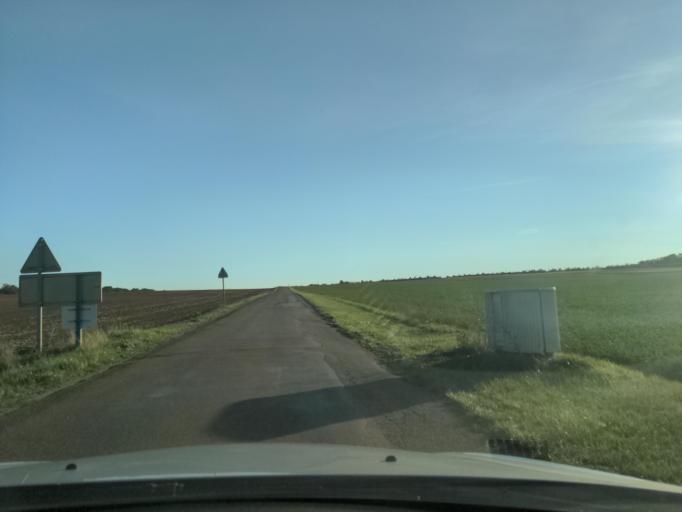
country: FR
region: Bourgogne
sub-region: Departement de la Cote-d'Or
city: Ruffey-les-Echirey
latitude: 47.3958
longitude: 5.0830
